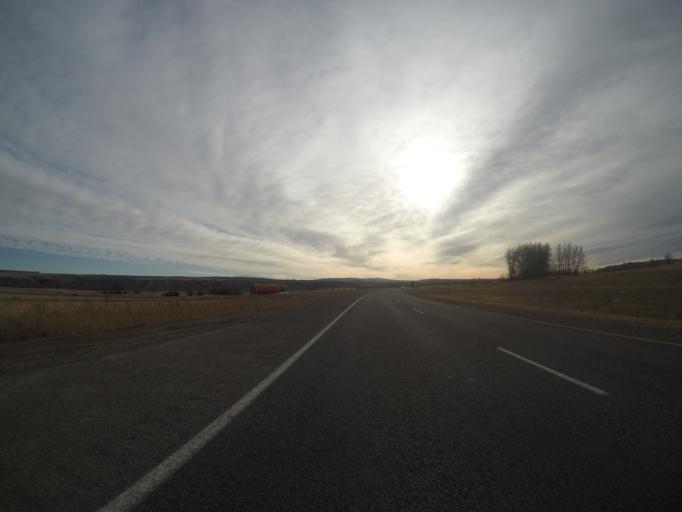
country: US
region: Montana
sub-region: Yellowstone County
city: Laurel
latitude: 45.5387
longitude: -108.8522
